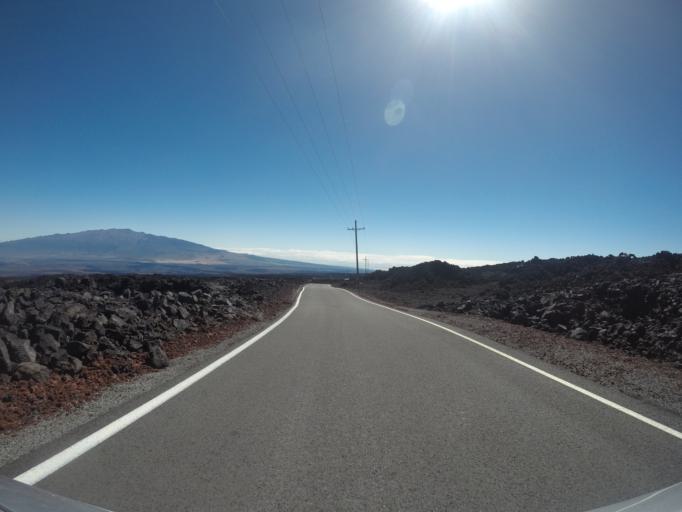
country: US
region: Hawaii
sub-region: Hawaii County
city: Volcano
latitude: 19.5534
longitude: -155.5385
